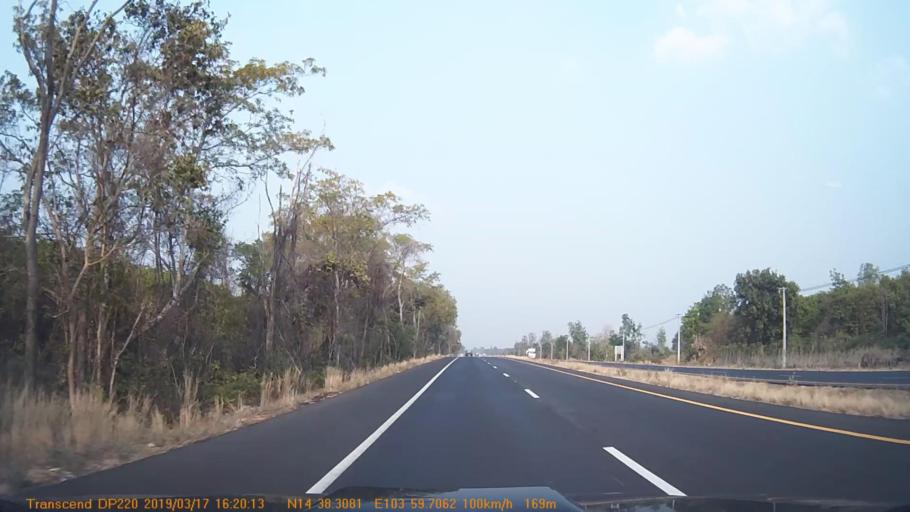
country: TH
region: Surin
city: Bua Chet
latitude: 14.6386
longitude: 103.9954
